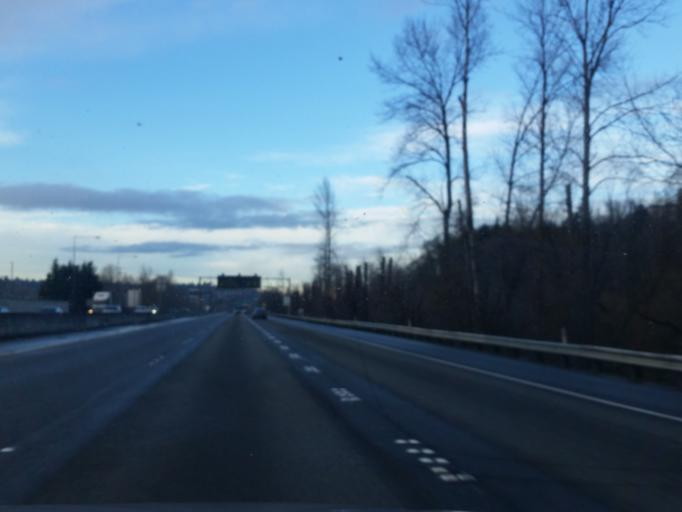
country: US
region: Washington
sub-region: King County
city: Renton
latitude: 47.4565
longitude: -122.2163
